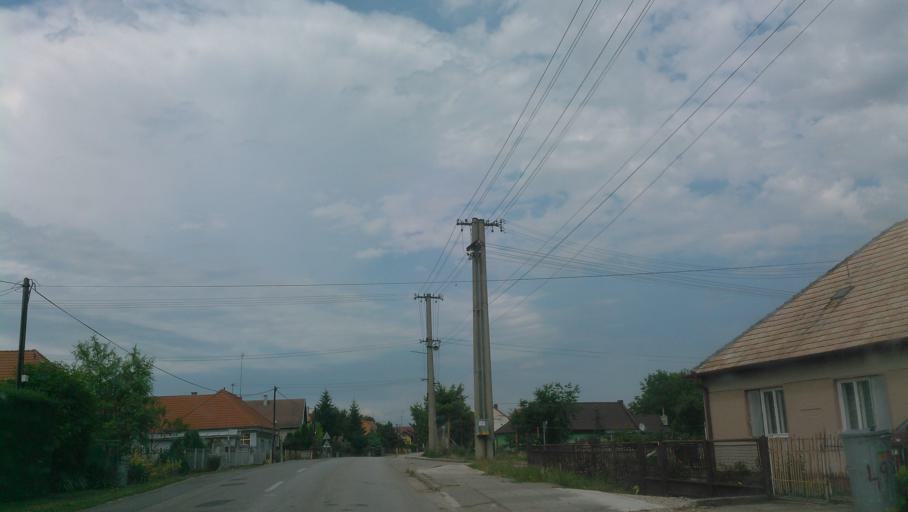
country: SK
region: Trnavsky
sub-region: Okres Trnava
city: Piestany
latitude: 48.4943
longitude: 17.9740
